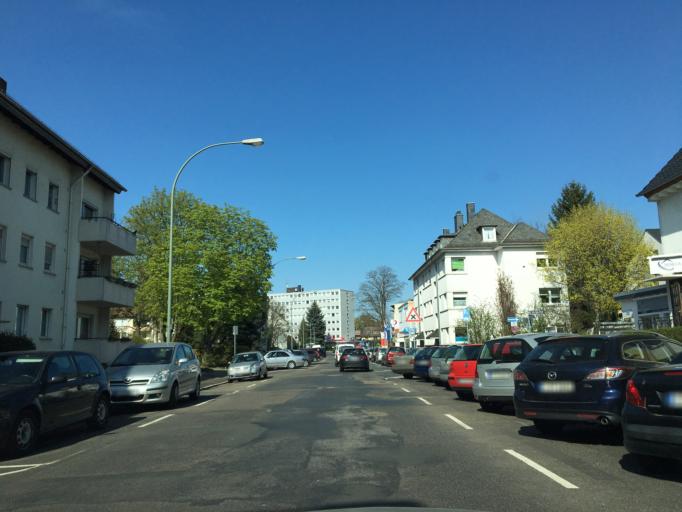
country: DE
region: Hesse
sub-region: Regierungsbezirk Darmstadt
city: Frankfurt am Main
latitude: 50.1471
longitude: 8.6555
